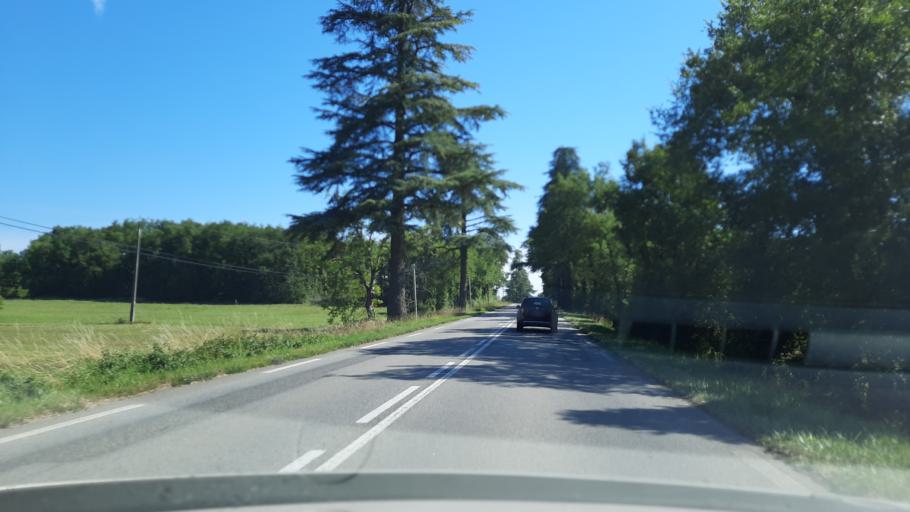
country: FR
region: Midi-Pyrenees
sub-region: Departement du Tarn-et-Garonne
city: Caylus
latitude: 44.3024
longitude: 1.8778
